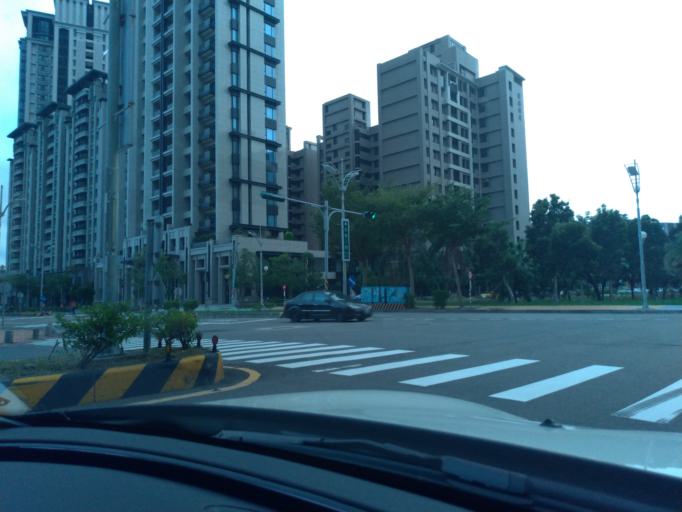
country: TW
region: Taiwan
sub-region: Hsinchu
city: Zhubei
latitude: 24.8163
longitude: 121.0176
